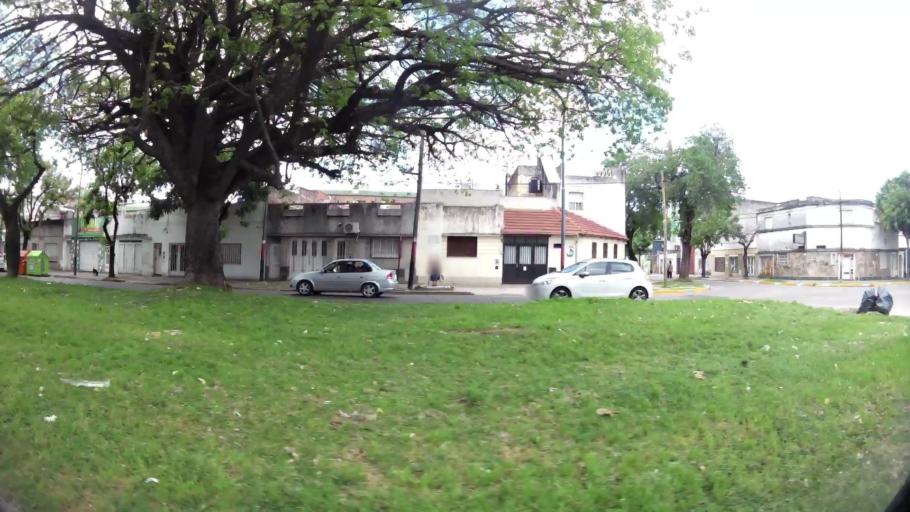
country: AR
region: Santa Fe
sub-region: Departamento de Rosario
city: Rosario
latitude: -32.9806
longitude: -60.6377
